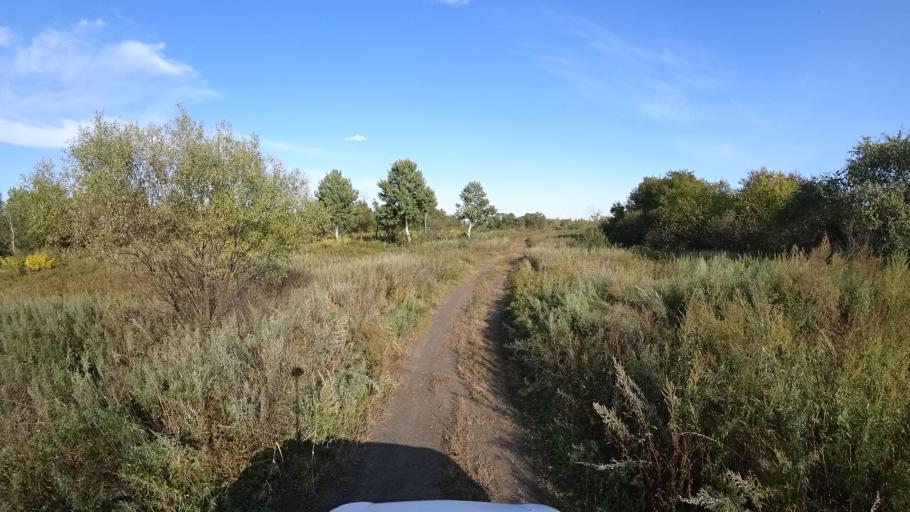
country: RU
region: Amur
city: Arkhara
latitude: 49.3496
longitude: 130.1220
